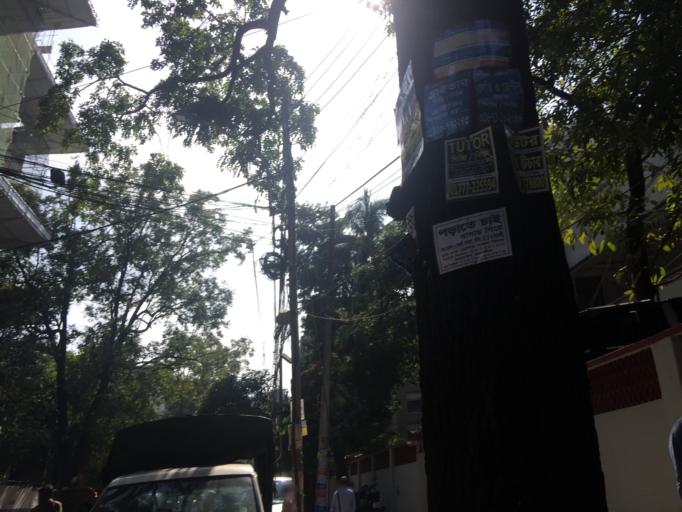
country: BD
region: Dhaka
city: Azimpur
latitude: 23.7407
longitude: 90.3804
